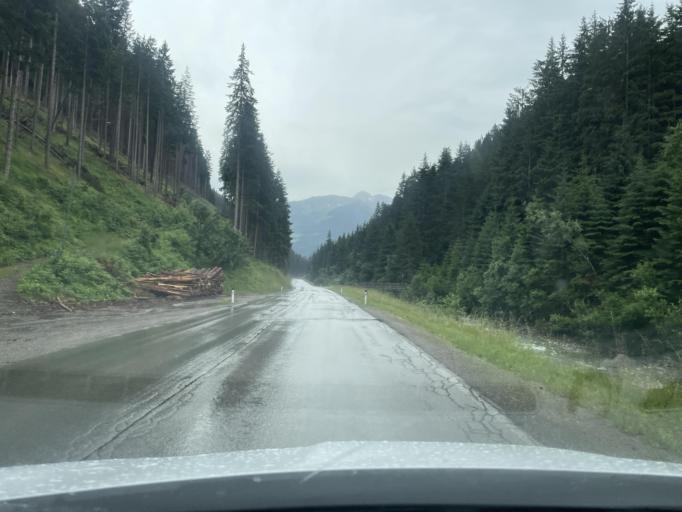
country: AT
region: Tyrol
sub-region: Politischer Bezirk Lienz
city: Ausservillgraten
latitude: 46.7771
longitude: 12.4278
